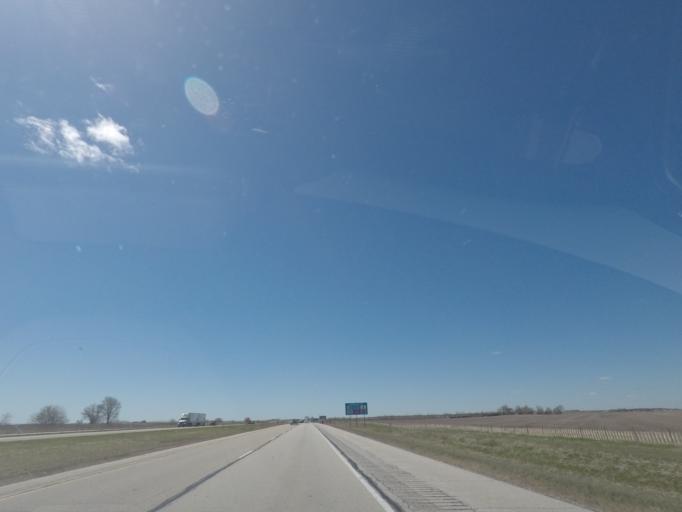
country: US
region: Illinois
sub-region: McLean County
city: Normal
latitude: 40.5542
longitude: -88.9152
